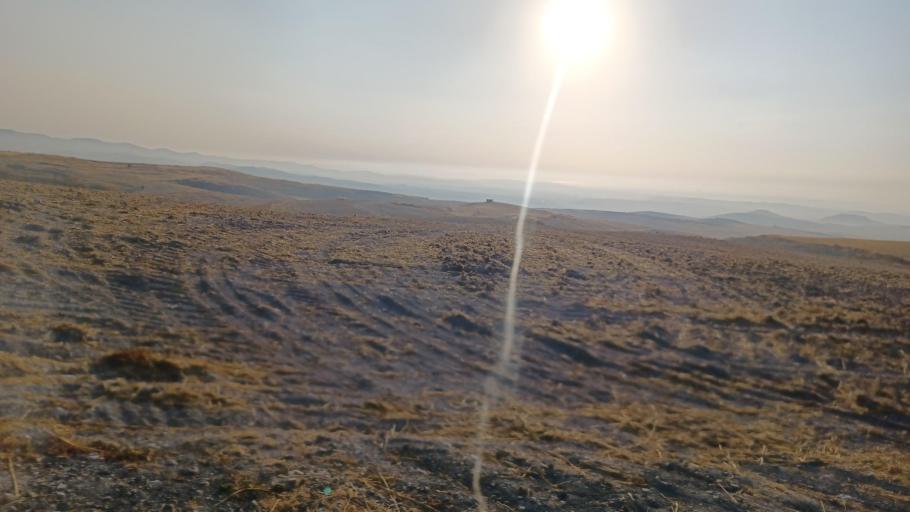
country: CY
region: Larnaka
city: Psevdas
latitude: 34.9115
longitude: 33.4892
